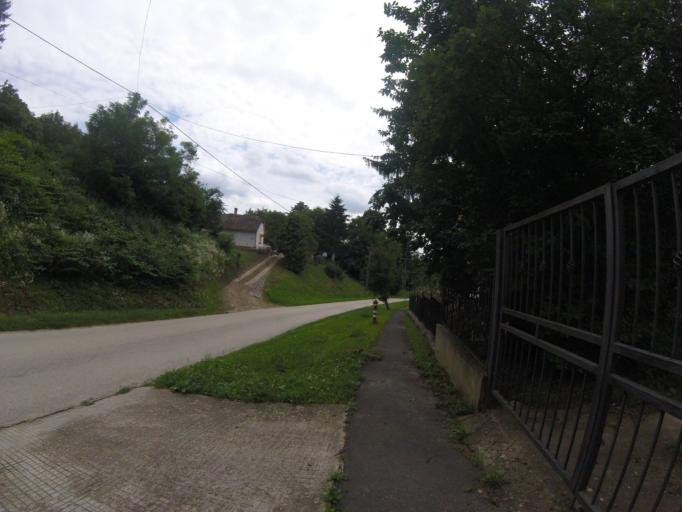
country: HU
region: Zala
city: Nagykanizsa
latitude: 46.5548
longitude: 17.0445
